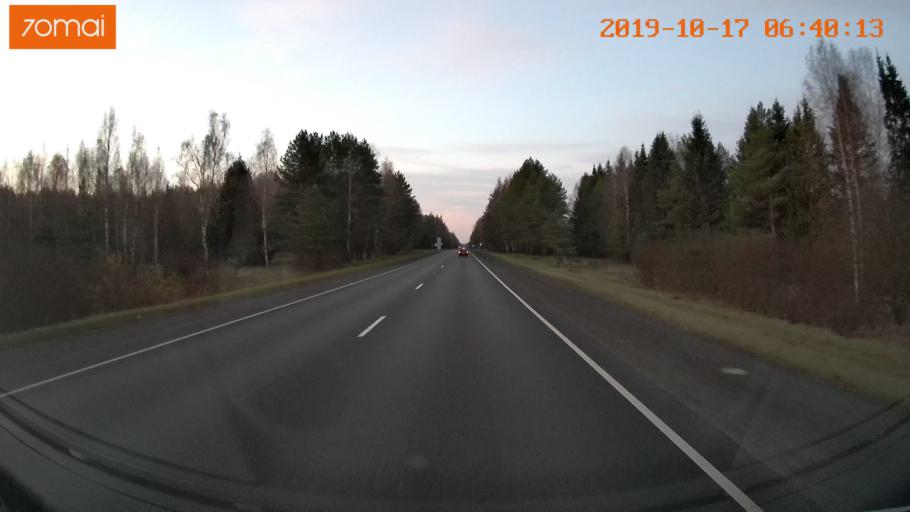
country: RU
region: Ivanovo
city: Novoye Leushino
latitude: 56.6322
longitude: 40.5716
